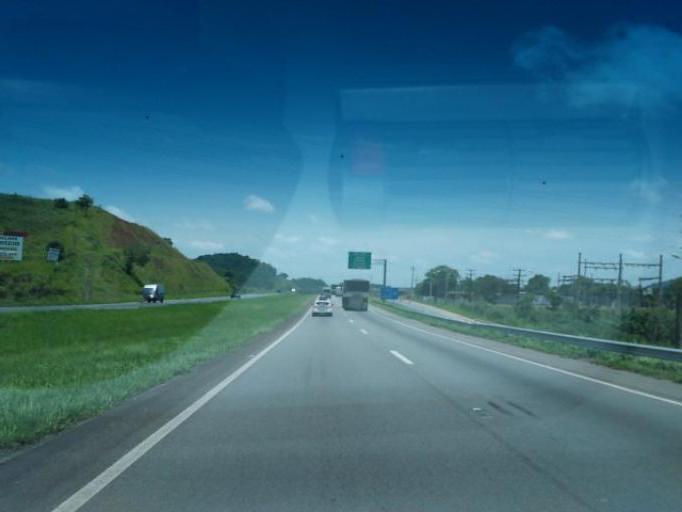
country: BR
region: Sao Paulo
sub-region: Juquia
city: Juquia
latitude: -24.3304
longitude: -47.6265
